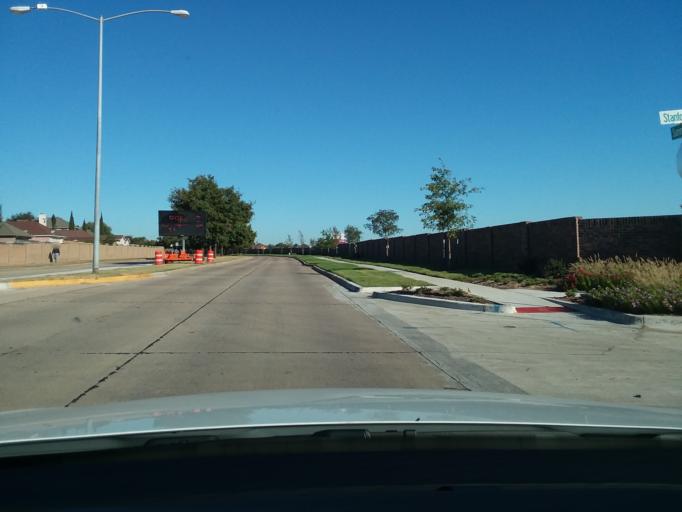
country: US
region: Texas
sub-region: Denton County
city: Lewisville
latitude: 33.0486
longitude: -97.0161
